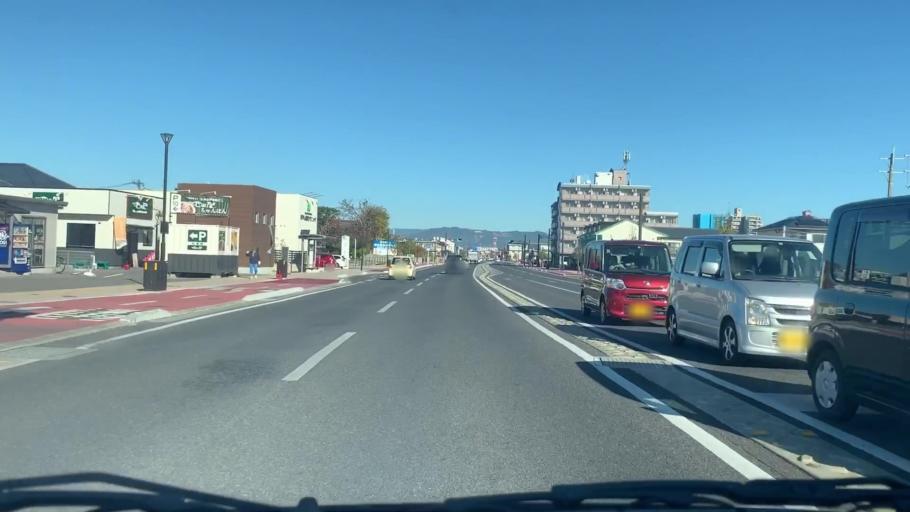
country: JP
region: Saga Prefecture
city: Saga-shi
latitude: 33.2451
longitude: 130.2933
